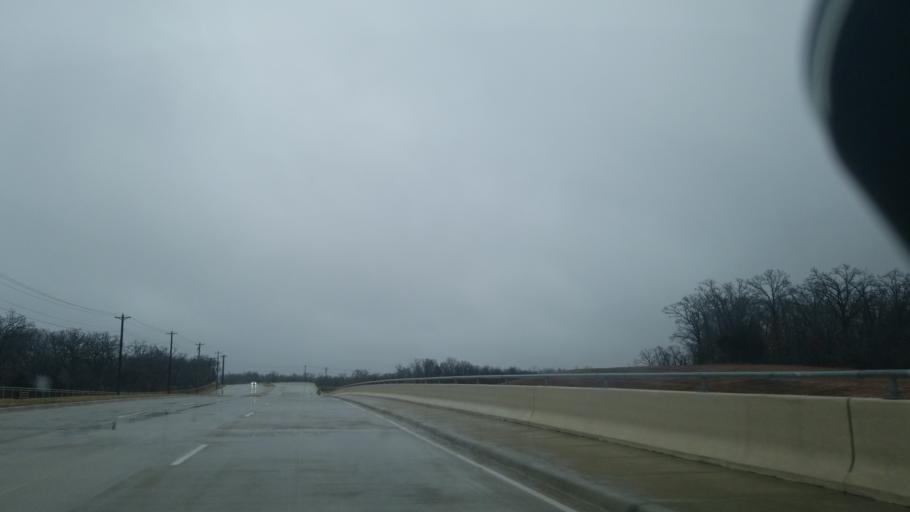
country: US
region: Texas
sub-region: Denton County
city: Corinth
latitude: 33.1394
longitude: -97.0959
